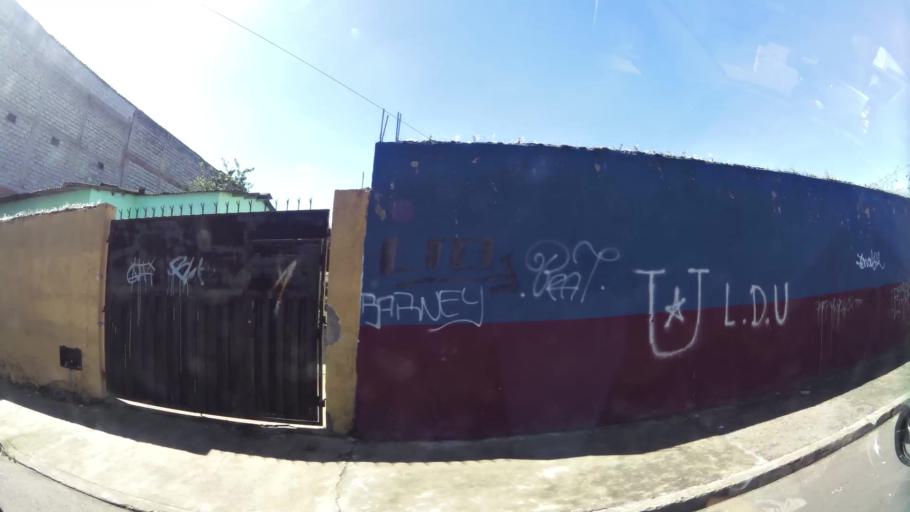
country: EC
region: Pichincha
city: Quito
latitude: -0.2796
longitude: -78.5571
